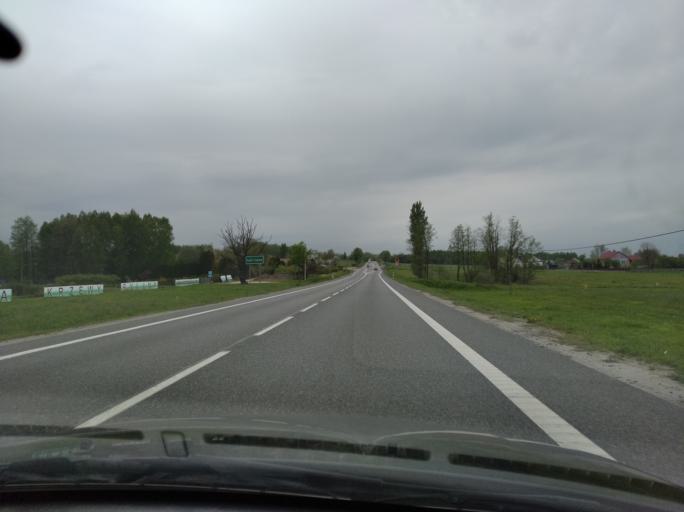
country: PL
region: Subcarpathian Voivodeship
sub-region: Powiat debicki
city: Leki Dolne
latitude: 50.0058
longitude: 21.2318
